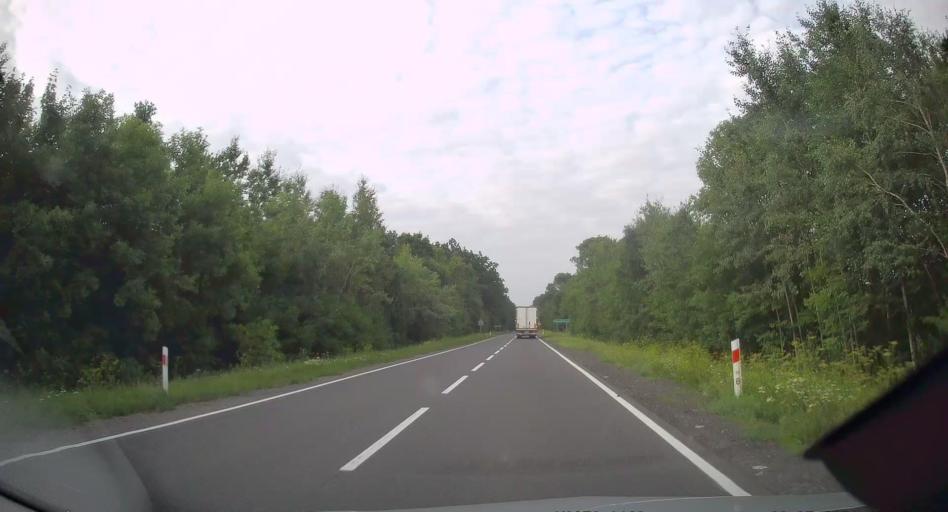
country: PL
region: Silesian Voivodeship
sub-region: Powiat czestochowski
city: Klomnice
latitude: 50.9474
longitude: 19.3953
